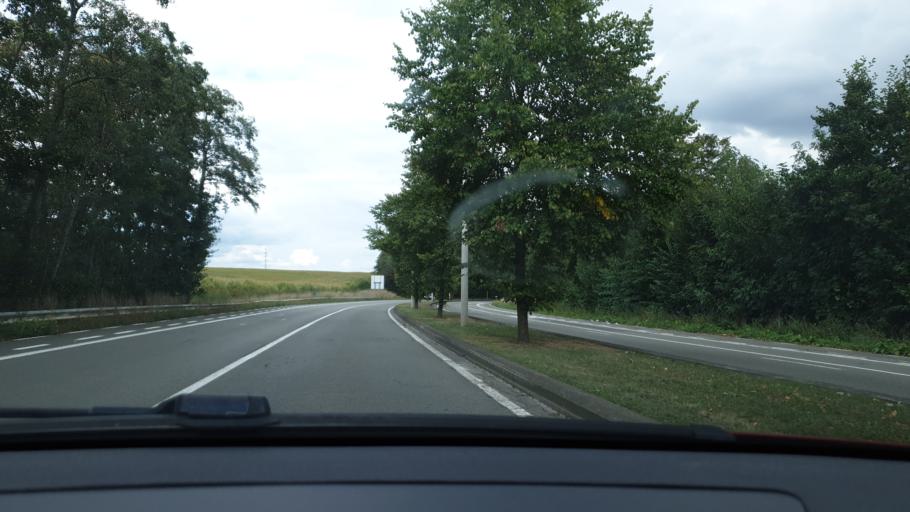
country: BE
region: Wallonia
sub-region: Province du Hainaut
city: Ath
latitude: 50.6376
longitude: 3.7642
